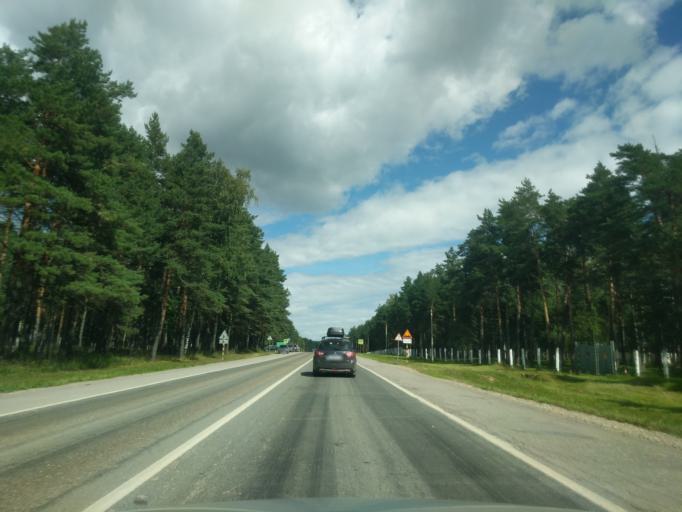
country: RU
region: Jaroslavl
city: Levashevo
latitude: 57.6744
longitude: 40.5860
